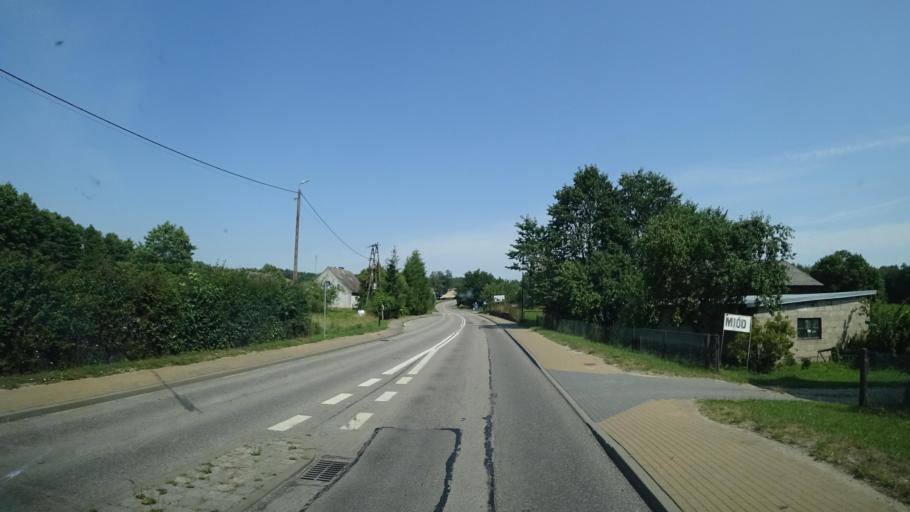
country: PL
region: Pomeranian Voivodeship
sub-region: Powiat koscierski
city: Dziemiany
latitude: 53.9701
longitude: 17.7635
